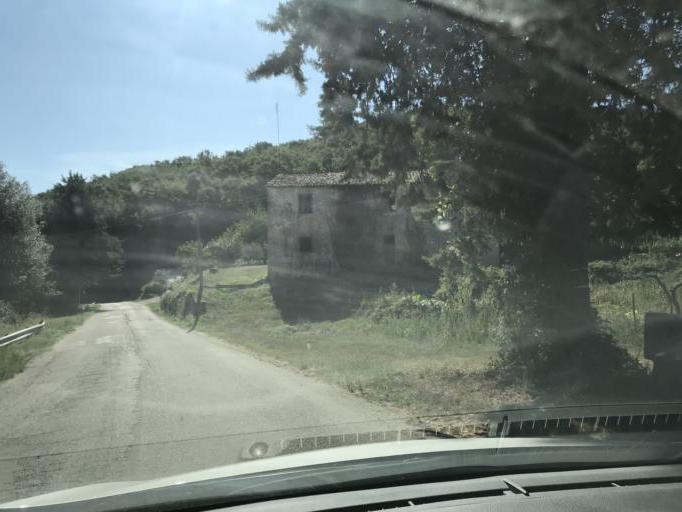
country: IT
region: Umbria
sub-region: Provincia di Terni
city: Avigliano Umbro
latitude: 42.6163
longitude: 12.4057
